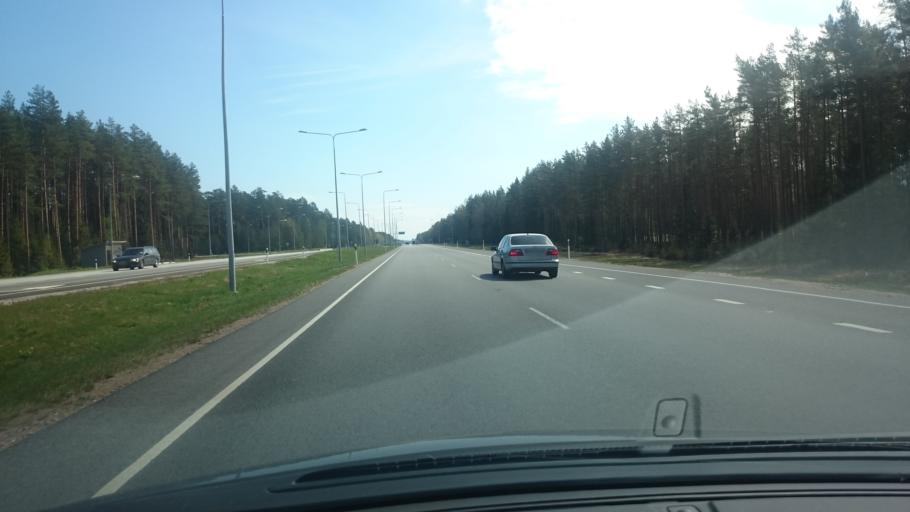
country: EE
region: Harju
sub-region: Loksa linn
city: Loksa
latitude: 59.4624
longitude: 25.6339
